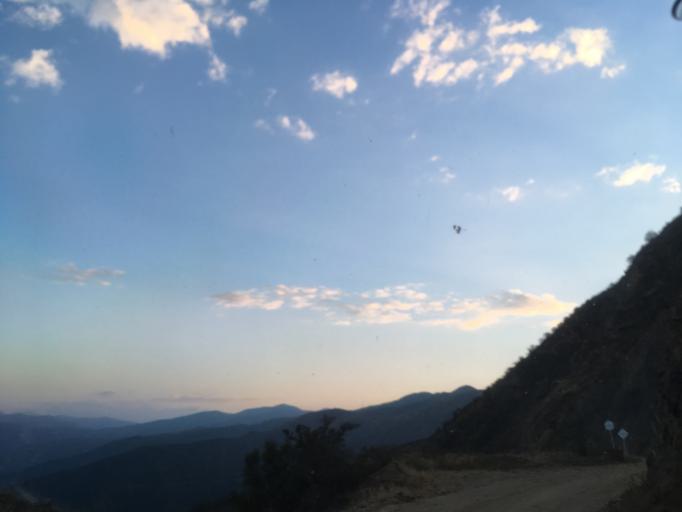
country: CO
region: Santander
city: Aratoca
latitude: 6.8006
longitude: -72.9918
